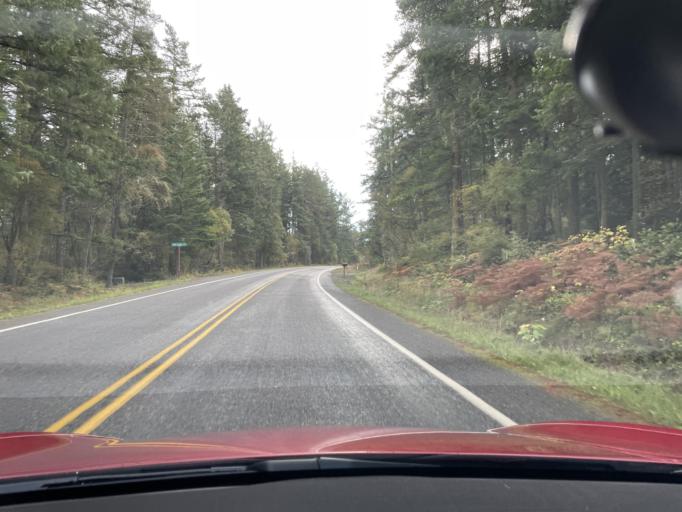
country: US
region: Washington
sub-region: San Juan County
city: Friday Harbor
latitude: 48.4895
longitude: -123.0314
